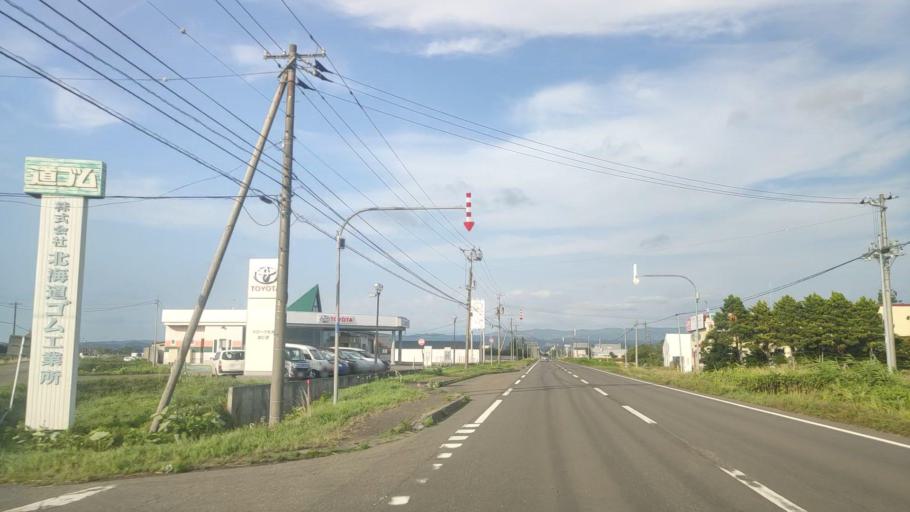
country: JP
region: Hokkaido
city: Iwamizawa
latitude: 43.0174
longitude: 141.7954
